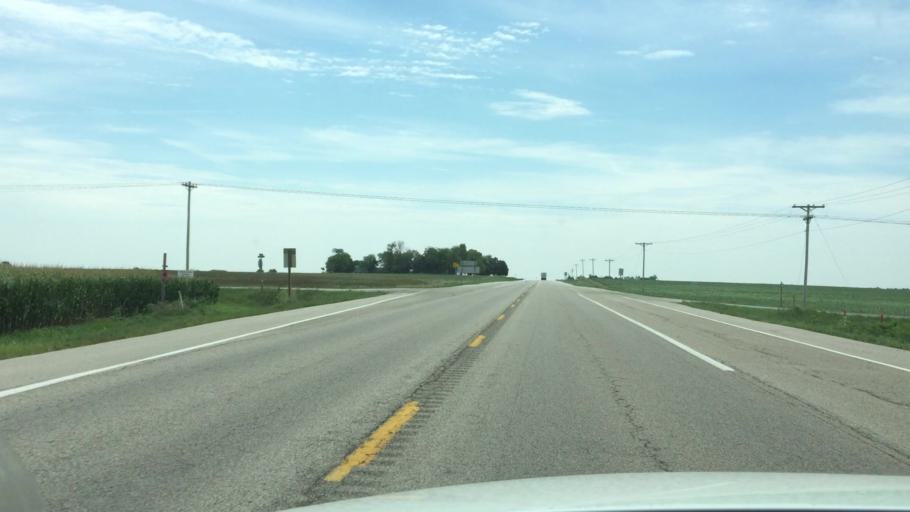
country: US
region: Kansas
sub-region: Nemaha County
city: Sabetha
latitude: 39.7549
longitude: -95.7297
